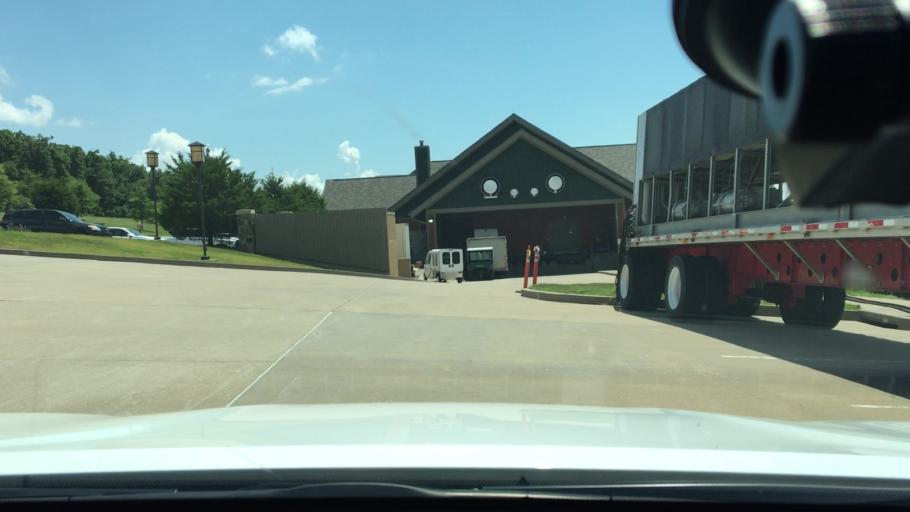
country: US
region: Arkansas
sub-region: Logan County
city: Paris
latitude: 35.1640
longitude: -93.6485
